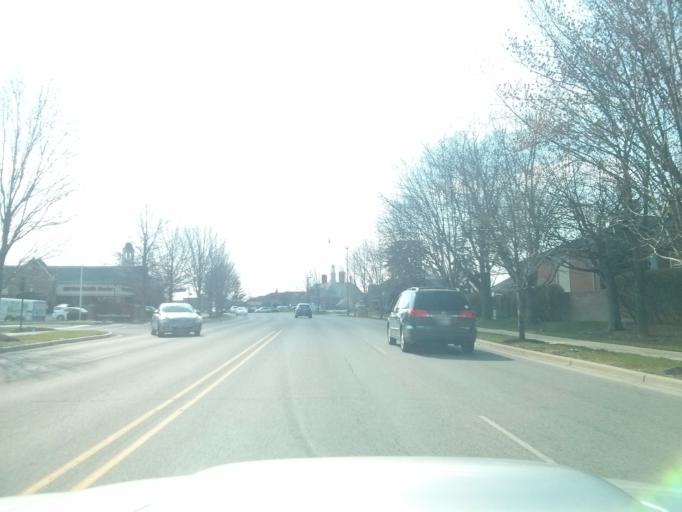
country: US
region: Indiana
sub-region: Hamilton County
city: Carmel
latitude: 39.9621
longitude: -86.1207
